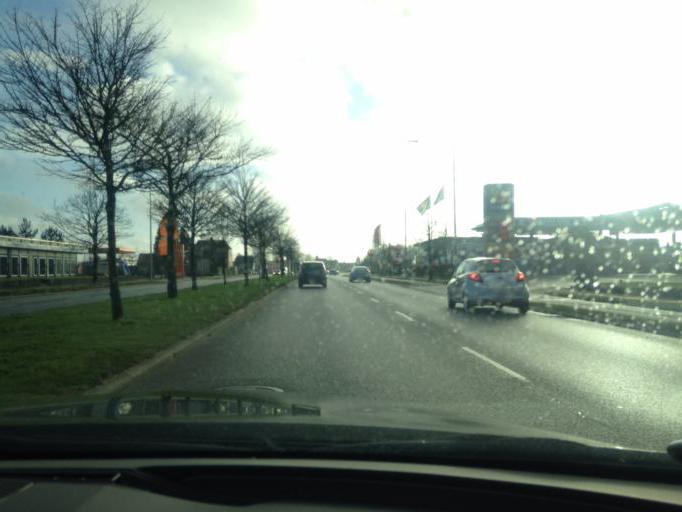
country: DK
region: South Denmark
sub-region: Kolding Kommune
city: Kolding
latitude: 55.5060
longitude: 9.4573
